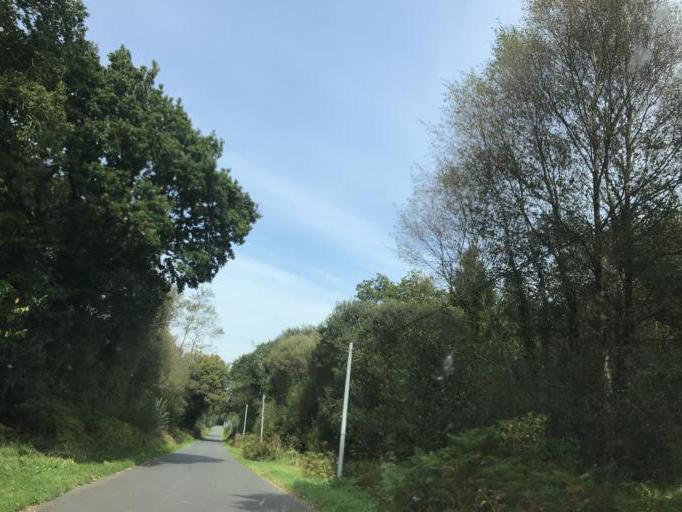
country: FR
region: Brittany
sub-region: Departement du Finistere
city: Brasparts
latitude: 48.3485
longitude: -3.8695
